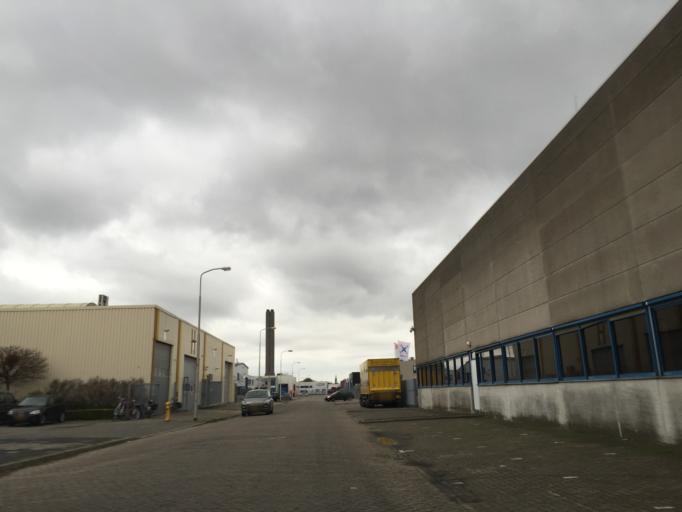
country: NL
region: South Holland
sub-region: Gemeente Delft
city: Delft
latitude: 51.9825
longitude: 4.3749
